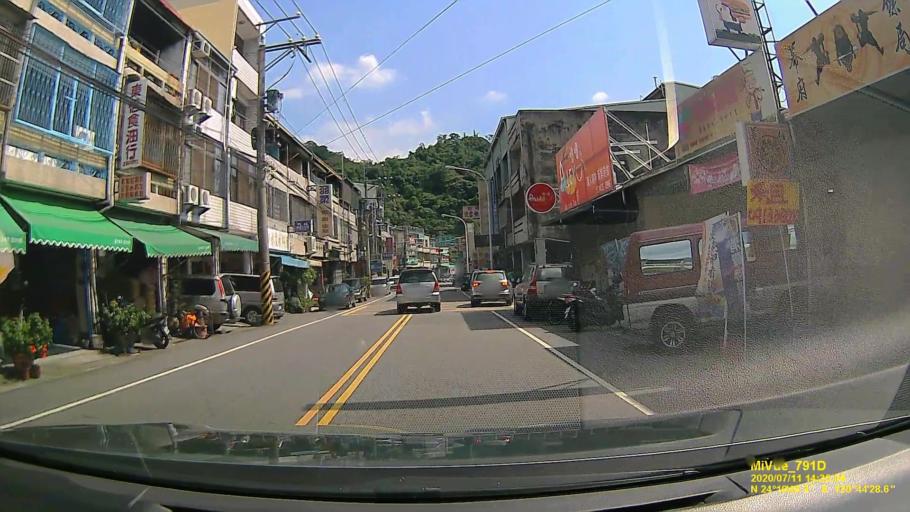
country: TW
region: Taiwan
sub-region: Taichung City
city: Taichung
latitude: 24.1794
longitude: 120.7412
